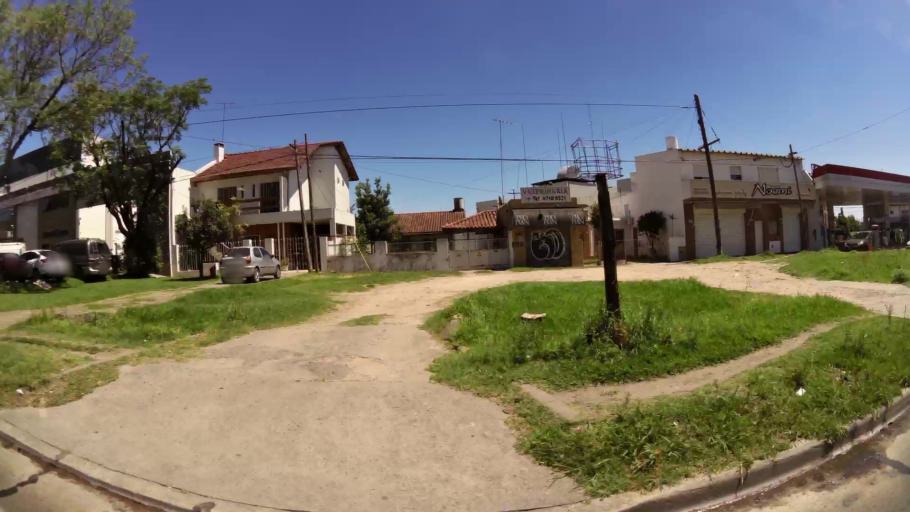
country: AR
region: Buenos Aires
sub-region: Partido de Tigre
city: Tigre
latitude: -34.4970
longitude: -58.5813
